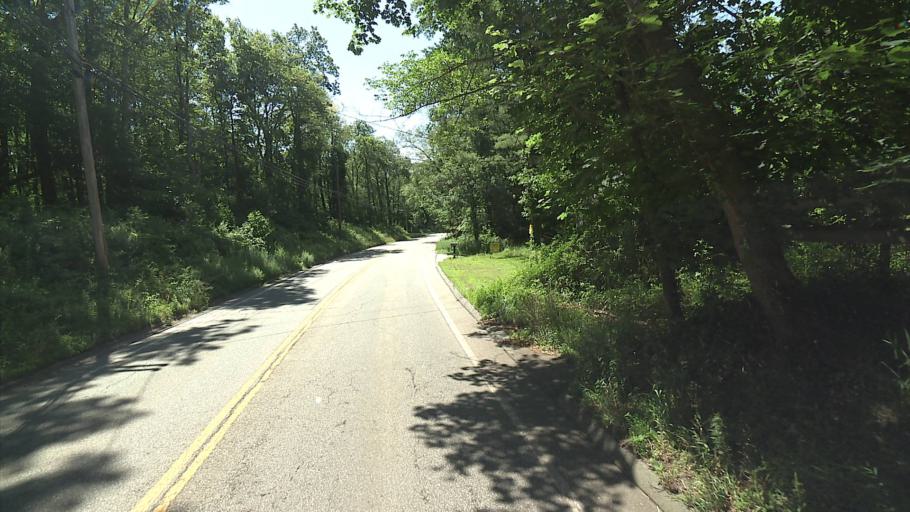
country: US
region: Connecticut
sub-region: Windham County
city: Willimantic
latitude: 41.6727
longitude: -72.2271
